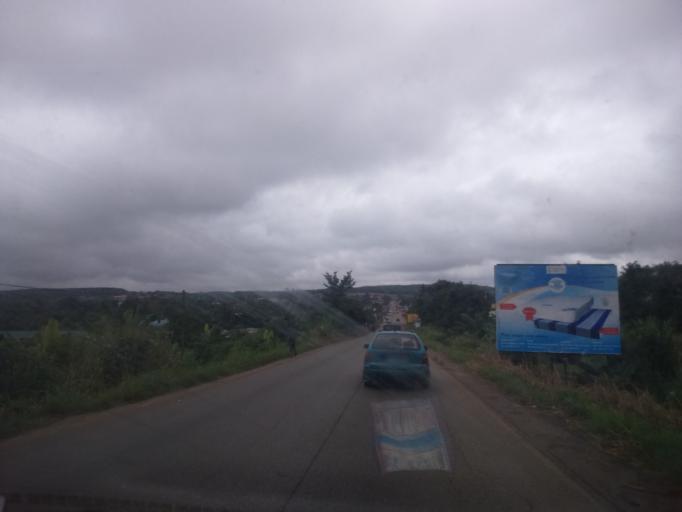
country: CI
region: Sud-Comoe
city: Bonoua
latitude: 5.2816
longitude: -3.5226
